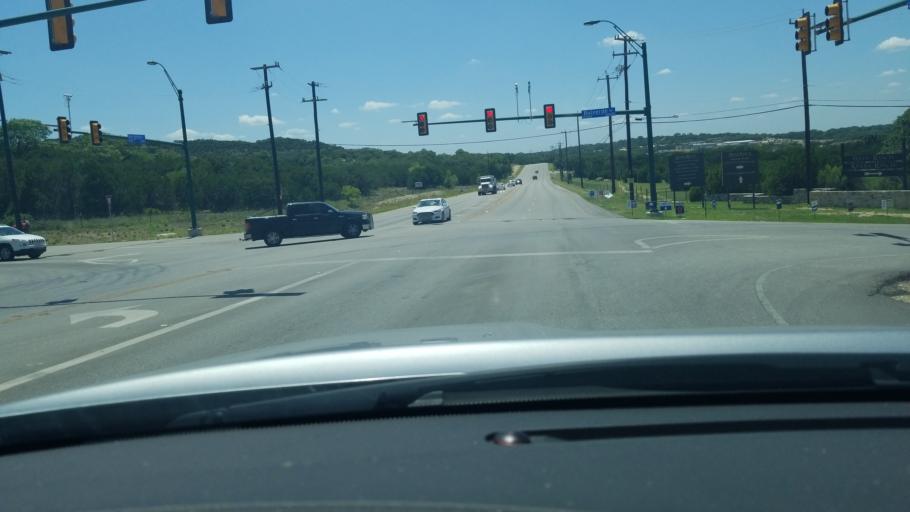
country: US
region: Texas
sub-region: Bexar County
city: Timberwood Park
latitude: 29.7141
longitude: -98.4542
